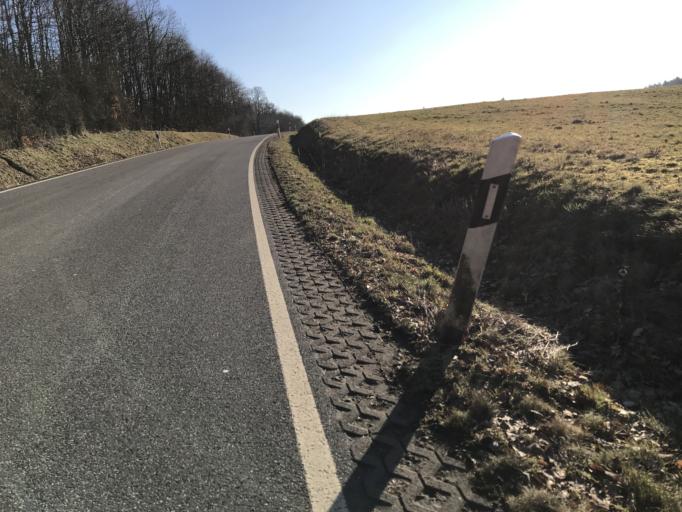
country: DE
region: Hesse
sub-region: Regierungsbezirk Giessen
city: Rabenau
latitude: 50.6646
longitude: 8.8532
